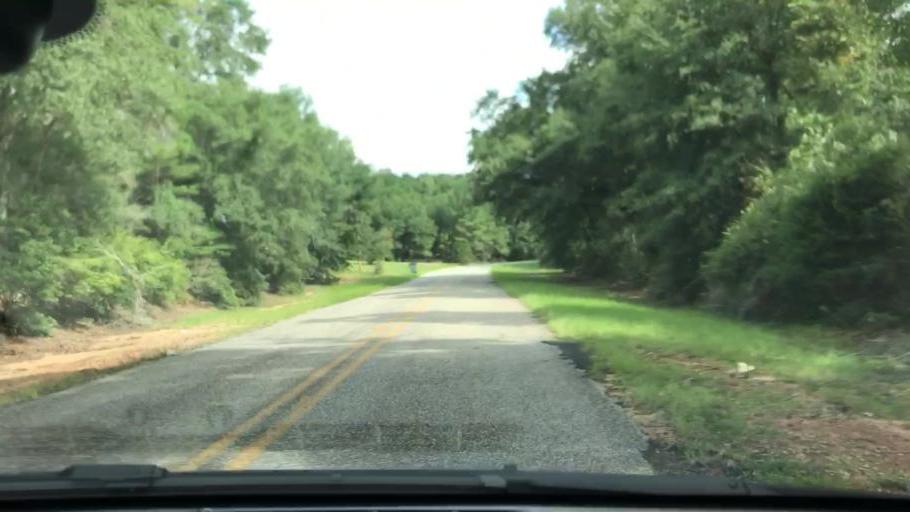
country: US
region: Georgia
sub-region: Early County
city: Blakely
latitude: 31.5046
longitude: -84.9455
